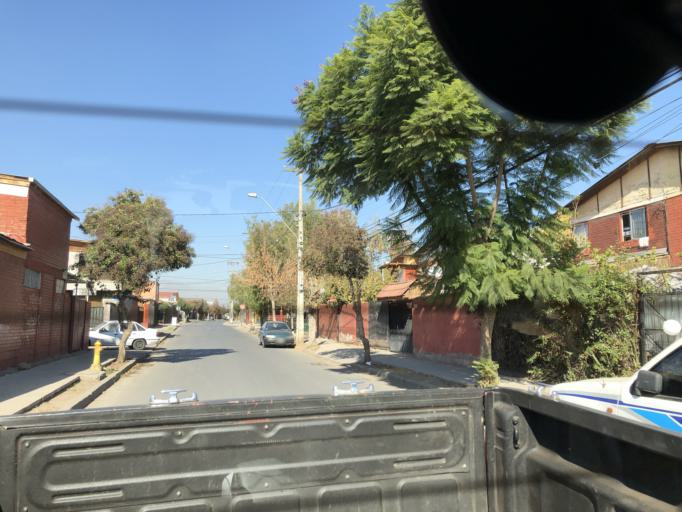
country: CL
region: Santiago Metropolitan
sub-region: Provincia de Cordillera
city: Puente Alto
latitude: -33.5650
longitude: -70.5771
